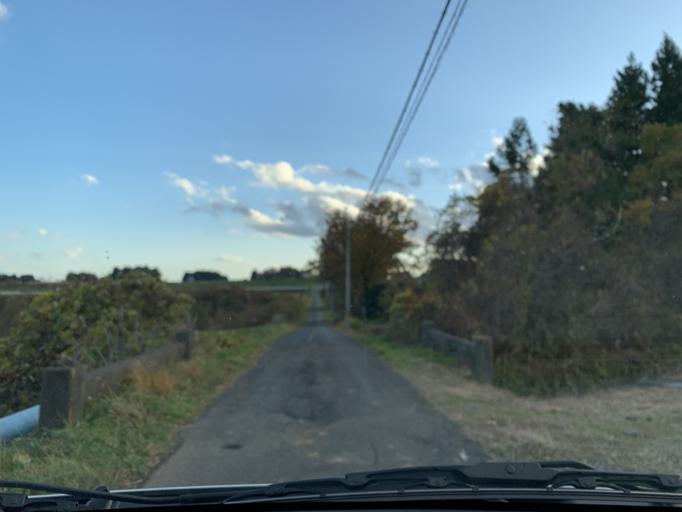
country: JP
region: Iwate
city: Mizusawa
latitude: 39.0970
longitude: 141.0391
